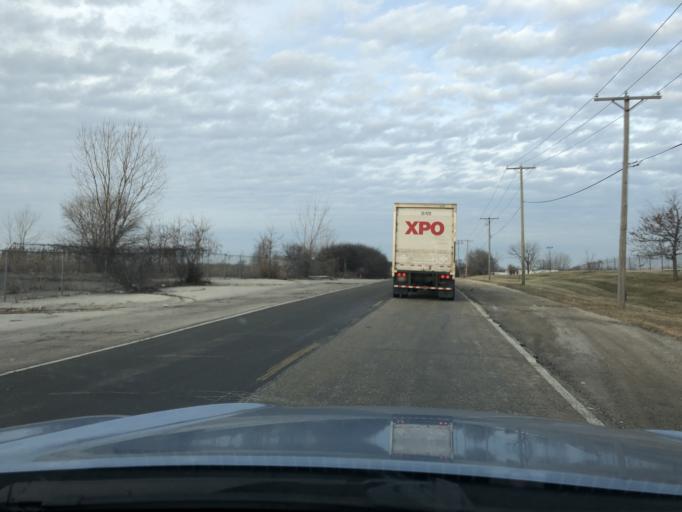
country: US
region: Illinois
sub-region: Cook County
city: Elk Grove Village
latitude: 42.0053
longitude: -87.9308
